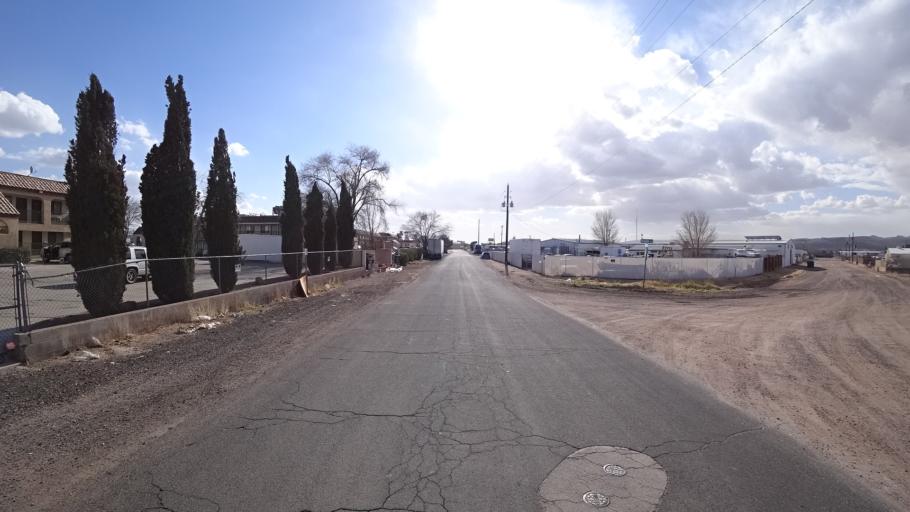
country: US
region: Arizona
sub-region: Mohave County
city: New Kingman-Butler
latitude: 35.2227
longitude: -114.0068
